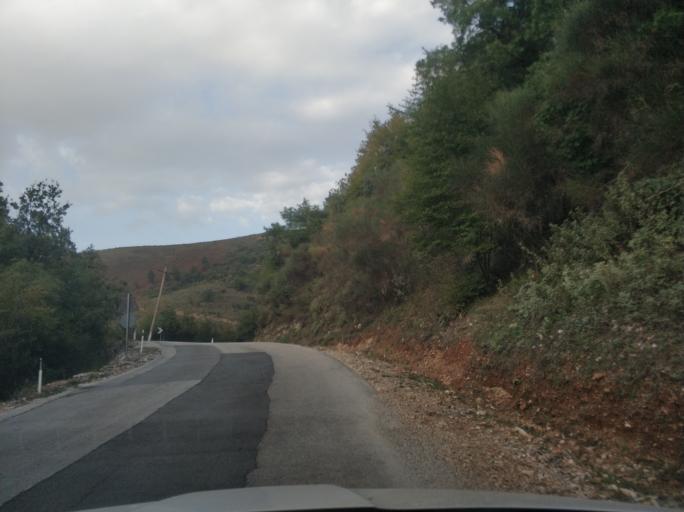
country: AL
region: Vlore
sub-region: Rrethi i Sarandes
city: Dhiver
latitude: 39.9208
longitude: 20.2014
